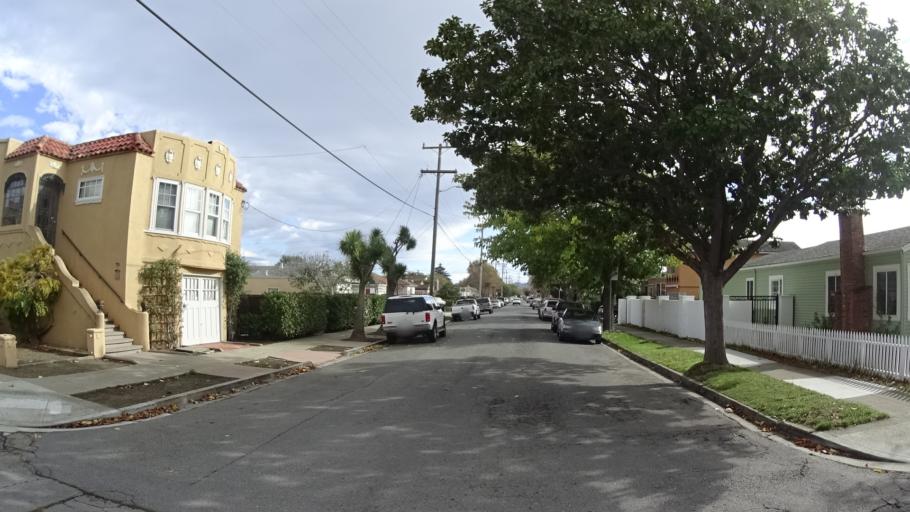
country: US
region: California
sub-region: San Mateo County
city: San Bruno
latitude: 37.6292
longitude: -122.4068
